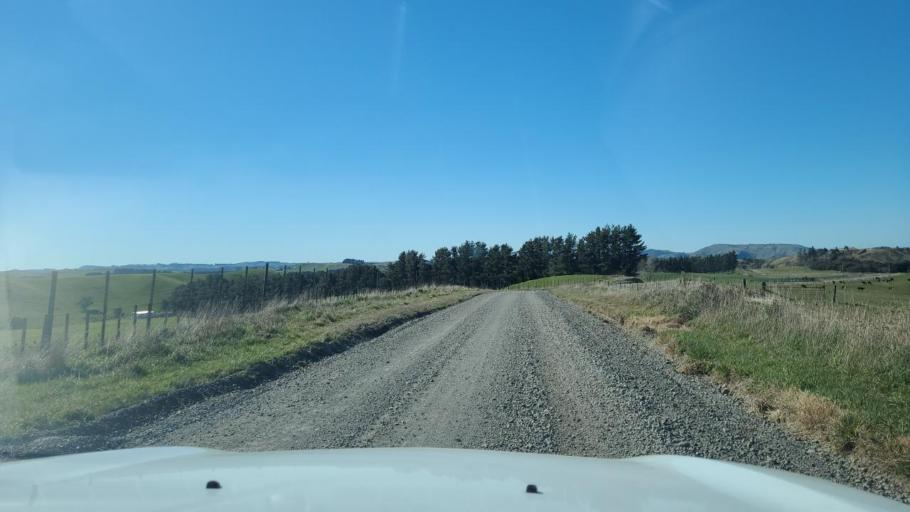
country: NZ
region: Hawke's Bay
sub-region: Napier City
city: Taradale
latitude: -39.4445
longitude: 176.5385
